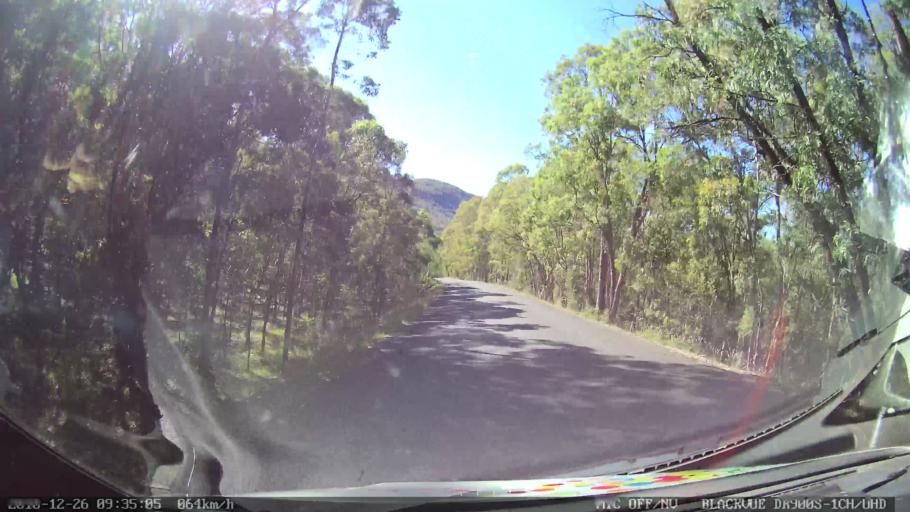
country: AU
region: New South Wales
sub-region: Mid-Western Regional
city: Kandos
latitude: -32.9115
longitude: 150.0389
